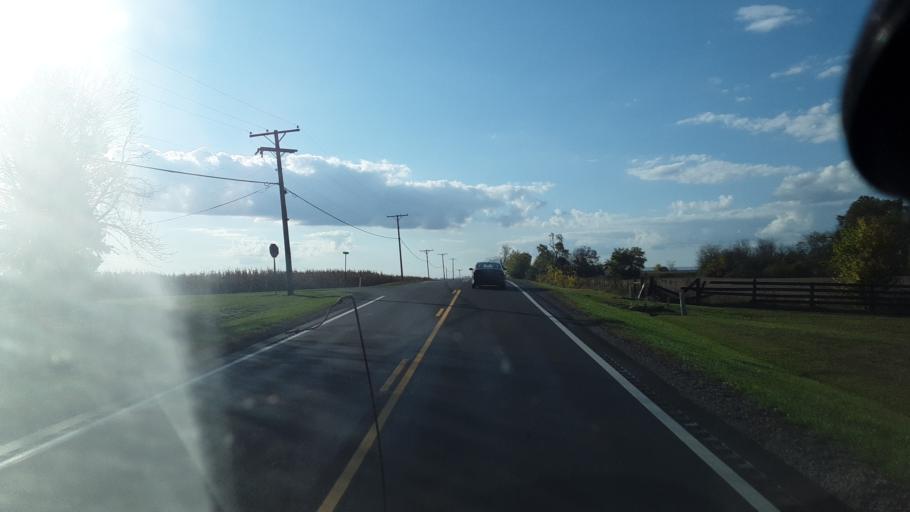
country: US
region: Ohio
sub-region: Fayette County
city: Jeffersonville
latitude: 39.6346
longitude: -83.5325
